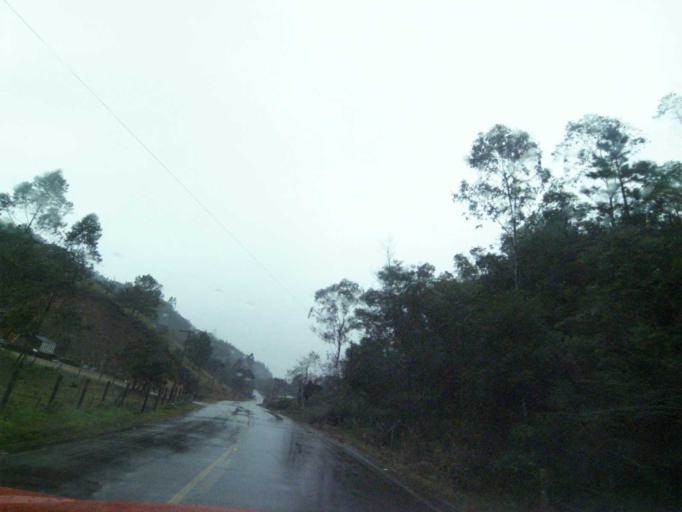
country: BR
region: Santa Catarina
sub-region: Anitapolis
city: Anitapolis
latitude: -27.8249
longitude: -49.0502
